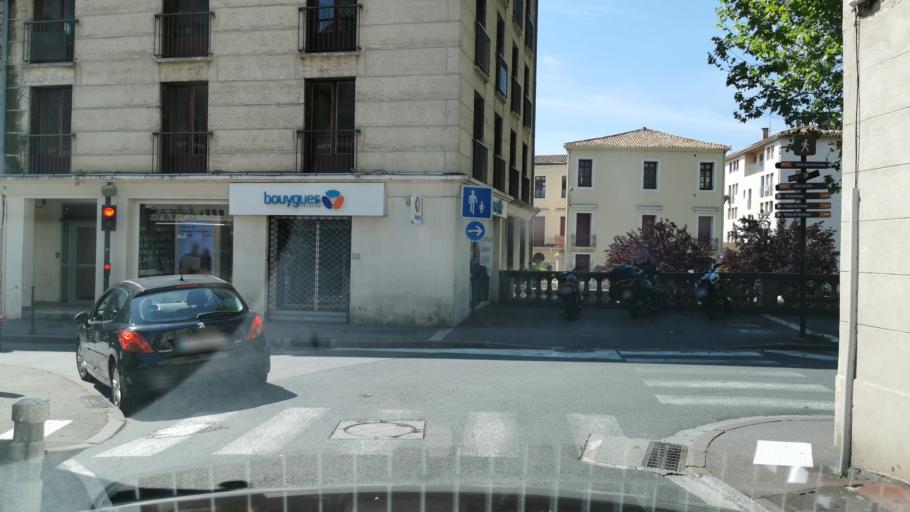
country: FR
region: Languedoc-Roussillon
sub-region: Departement de l'Aude
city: Narbonne
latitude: 43.1843
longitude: 3.0029
